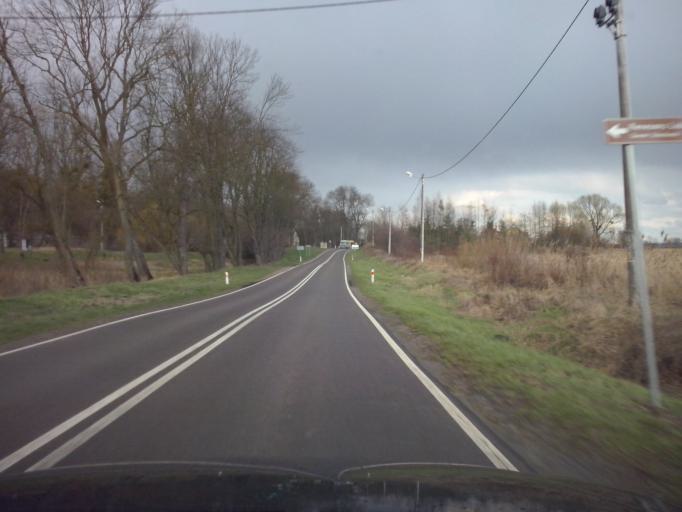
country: PL
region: Lublin Voivodeship
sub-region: Powiat krasnostawski
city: Krasnystaw
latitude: 51.0273
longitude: 23.2213
